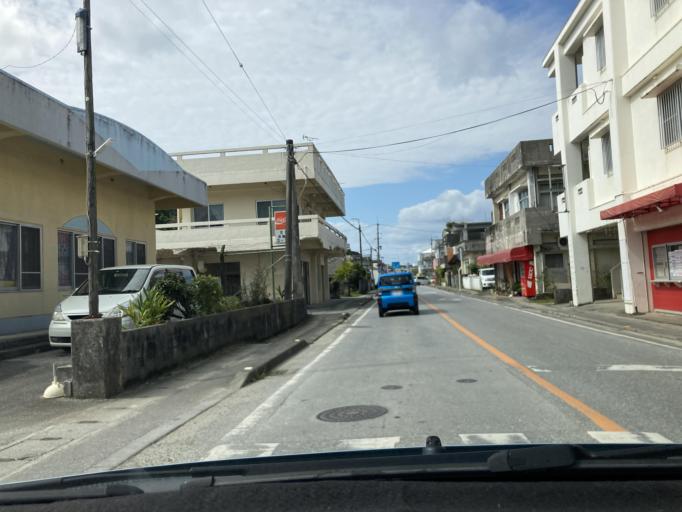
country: JP
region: Okinawa
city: Nago
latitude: 26.6578
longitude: 127.9019
